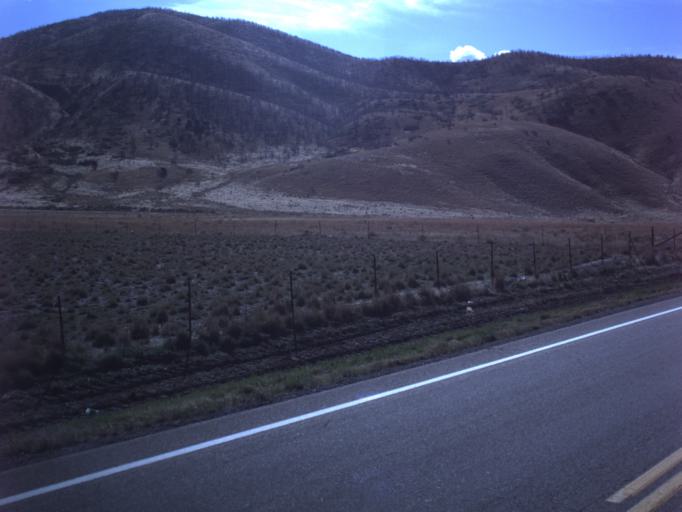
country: US
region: Utah
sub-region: Juab County
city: Nephi
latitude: 39.5351
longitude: -111.8637
